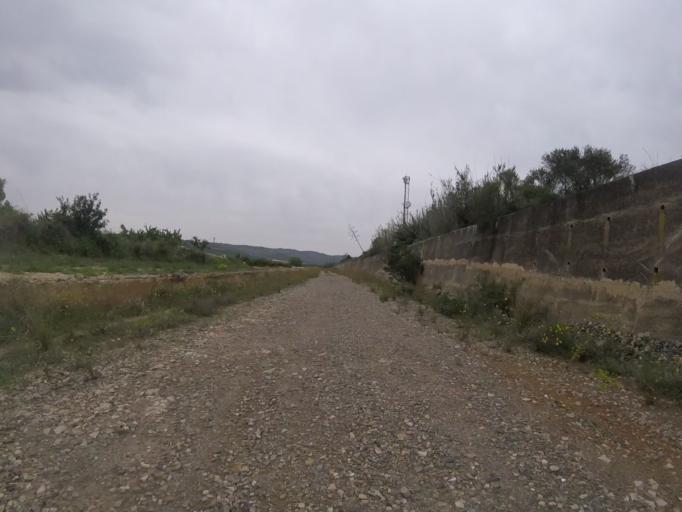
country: ES
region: Valencia
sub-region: Provincia de Castello
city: Alcoceber
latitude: 40.2640
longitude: 0.2579
